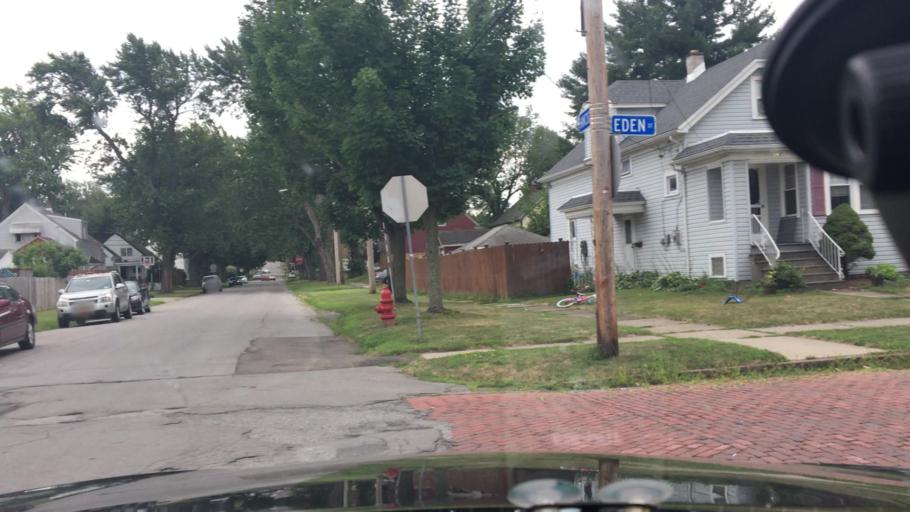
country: US
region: New York
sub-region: Erie County
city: Lackawanna
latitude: 42.8365
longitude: -78.8125
